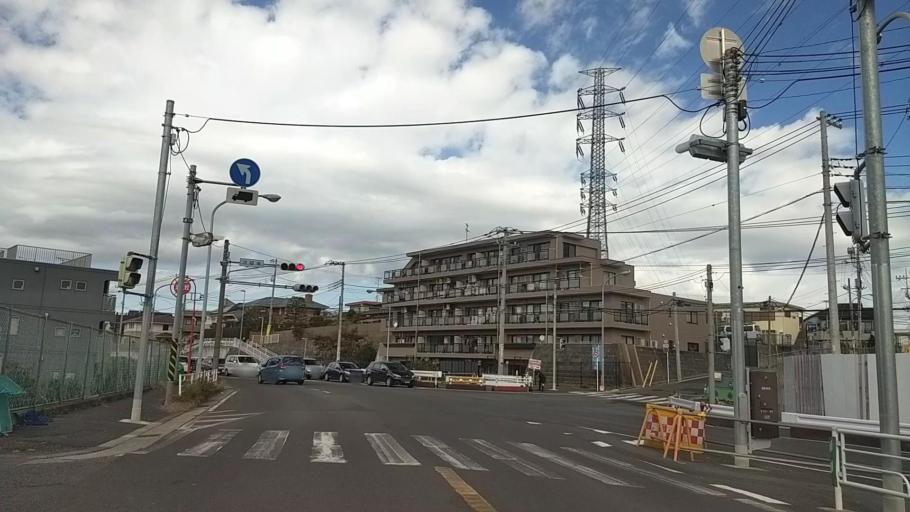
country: JP
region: Kanagawa
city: Yokohama
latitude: 35.5082
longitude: 139.6395
